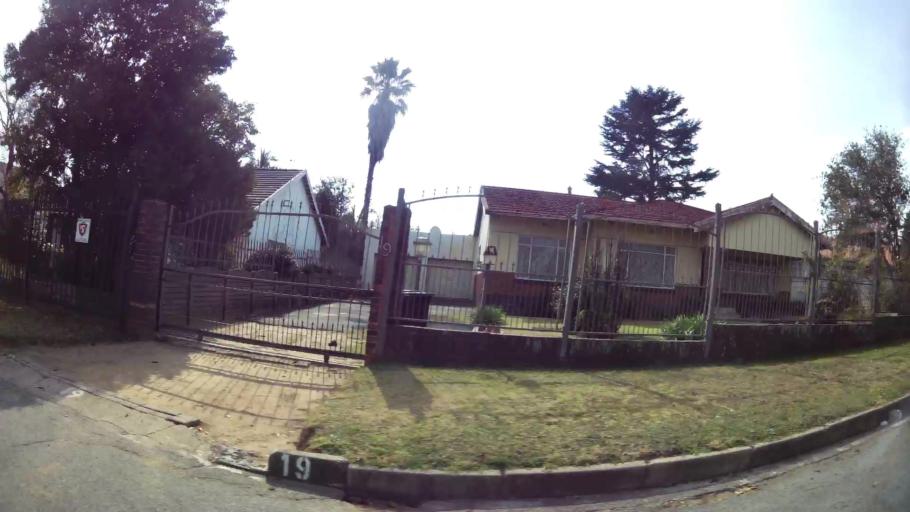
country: ZA
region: Gauteng
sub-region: City of Johannesburg Metropolitan Municipality
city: Modderfontein
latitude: -26.0889
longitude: 28.2246
